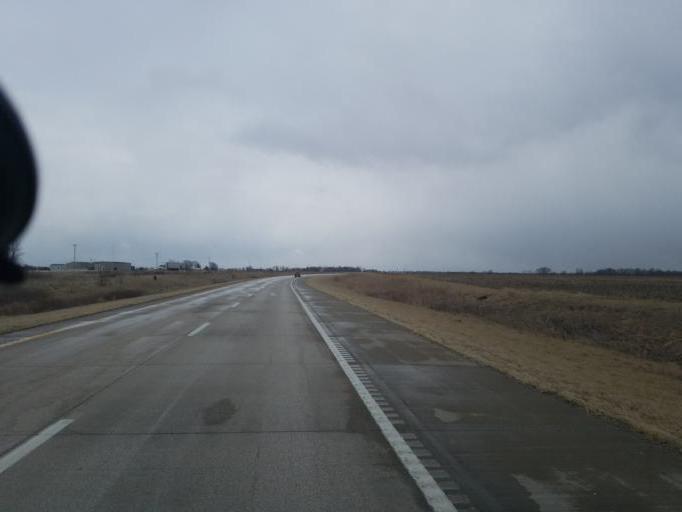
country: US
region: Missouri
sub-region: Randolph County
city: Moberly
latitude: 39.4907
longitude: -92.4349
